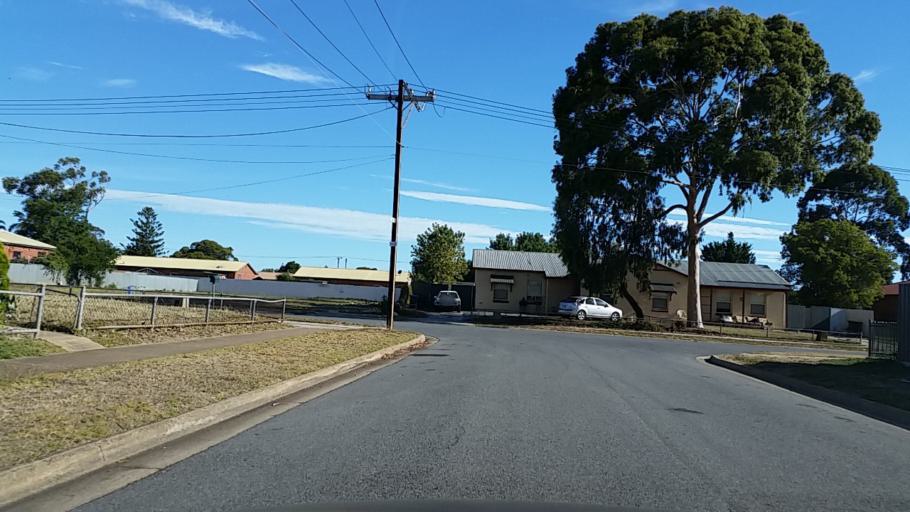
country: AU
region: South Australia
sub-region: Charles Sturt
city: Royal Park
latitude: -34.8818
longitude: 138.5104
